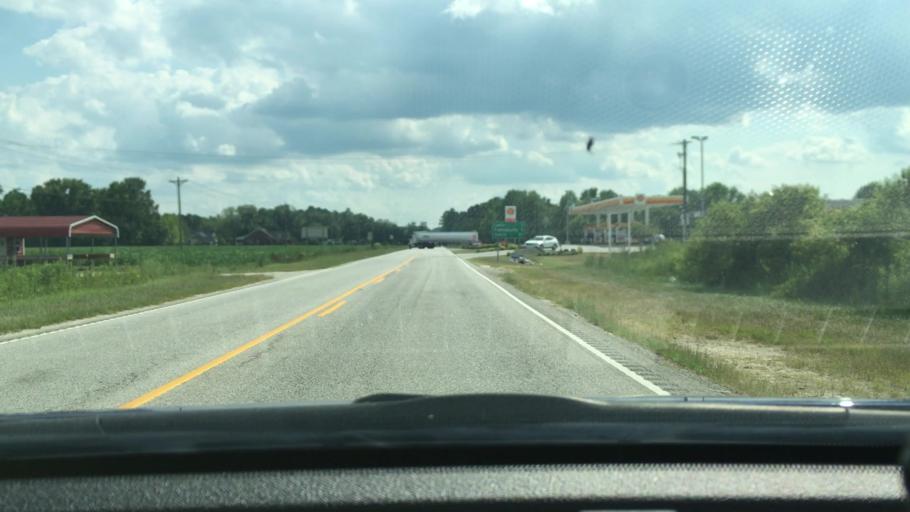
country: US
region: South Carolina
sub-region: Florence County
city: Timmonsville
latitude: 34.2042
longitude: -80.0291
